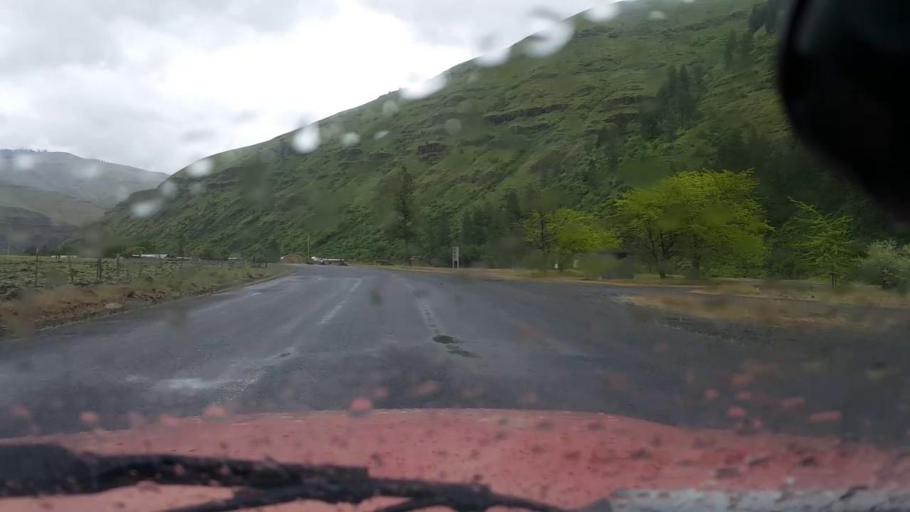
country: US
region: Washington
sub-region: Asotin County
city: Asotin
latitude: 46.0353
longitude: -117.2740
